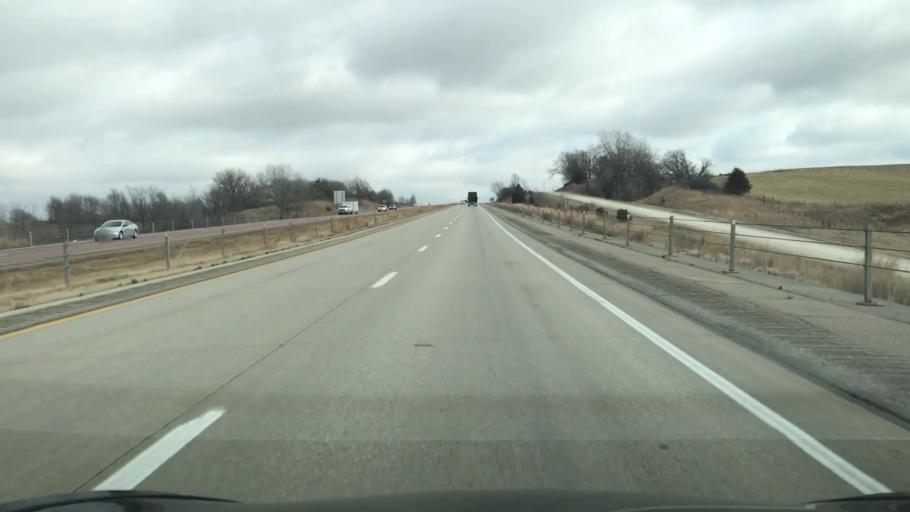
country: US
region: Iowa
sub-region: Guthrie County
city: Guthrie Center
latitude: 41.4962
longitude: -94.5341
